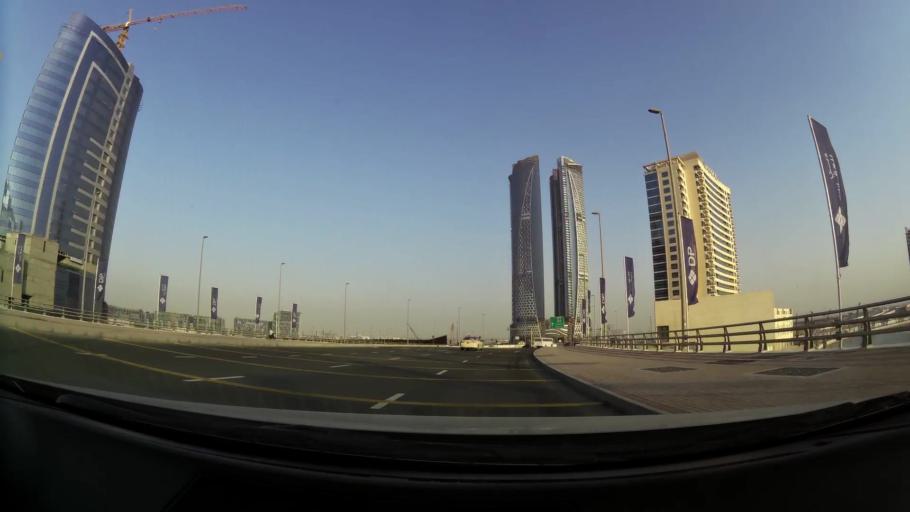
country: AE
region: Dubai
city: Dubai
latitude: 25.1909
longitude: 55.2889
